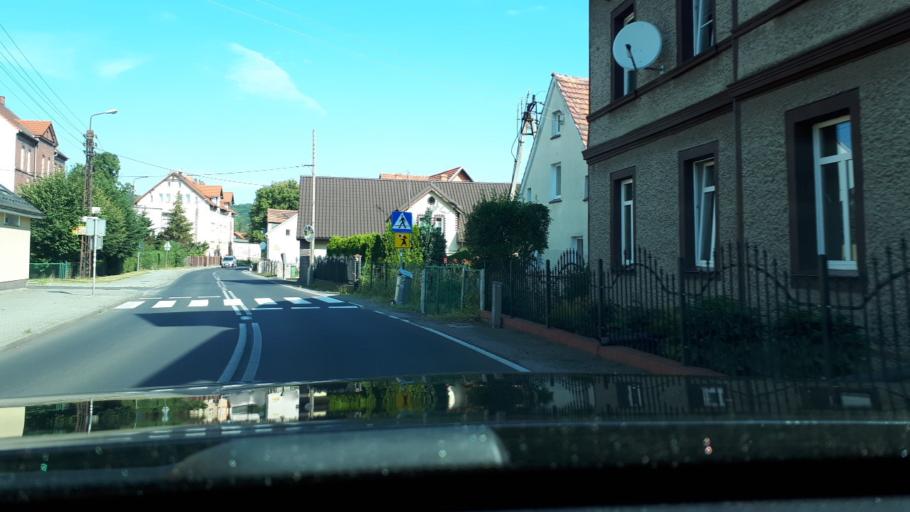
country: PL
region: Lower Silesian Voivodeship
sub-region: Powiat lubanski
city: Luban
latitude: 51.1044
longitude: 15.2941
